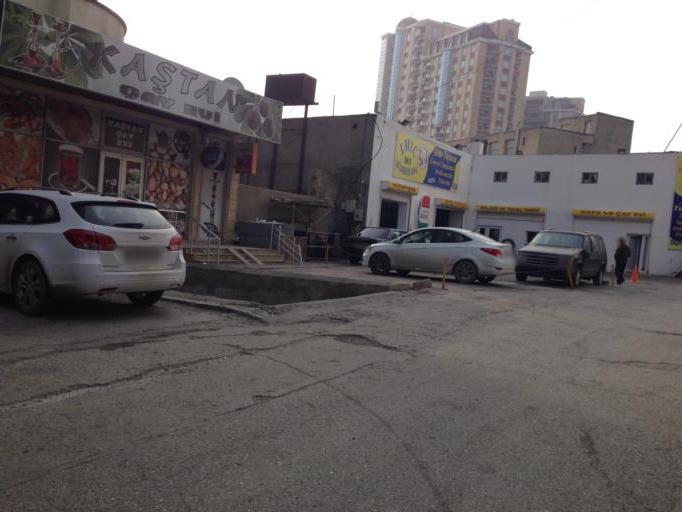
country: AZ
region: Baki
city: Baku
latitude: 40.3990
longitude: 49.8602
